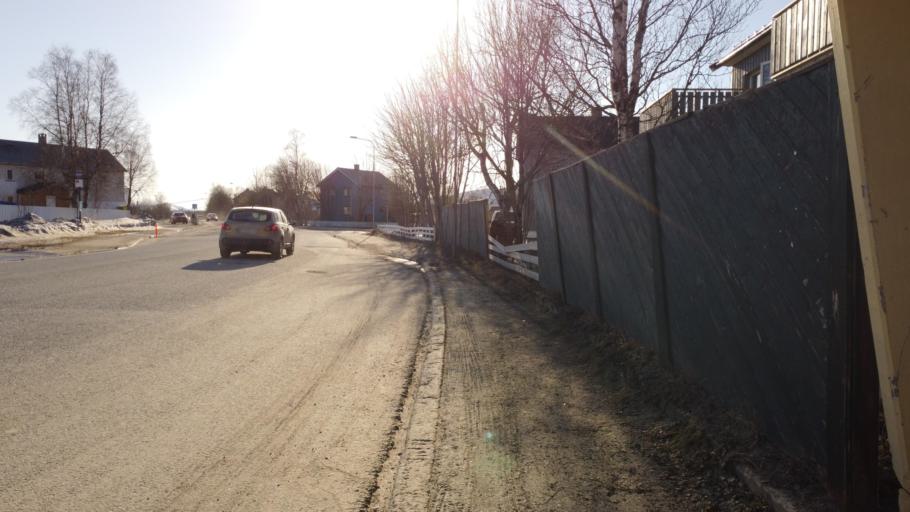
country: NO
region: Nordland
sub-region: Rana
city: Mo i Rana
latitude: 66.3197
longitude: 14.1864
